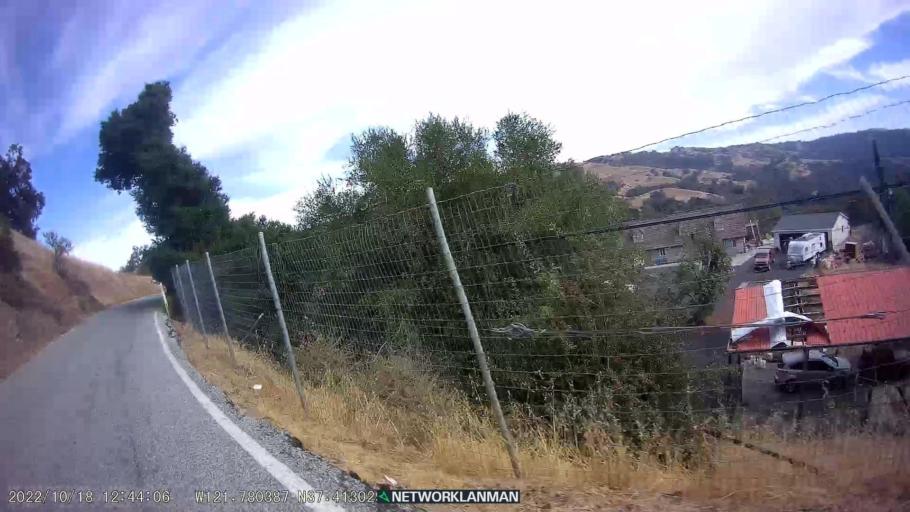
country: US
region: California
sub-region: Santa Clara County
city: East Foothills
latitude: 37.4132
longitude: -121.7802
